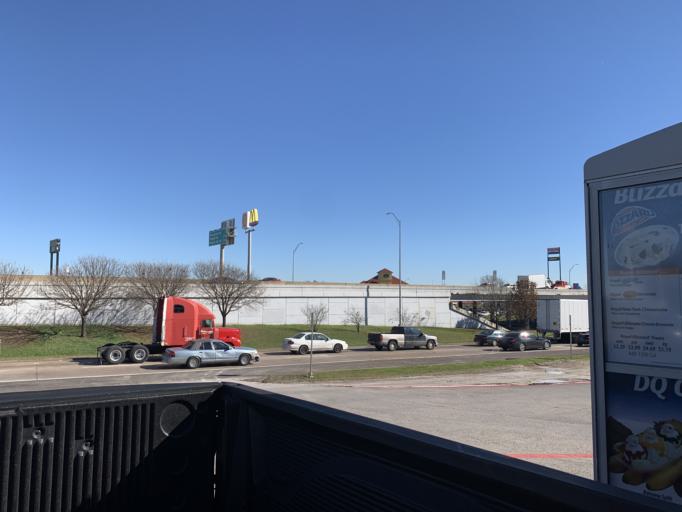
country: US
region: Texas
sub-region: Dallas County
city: Hutchins
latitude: 32.6496
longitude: -96.7087
